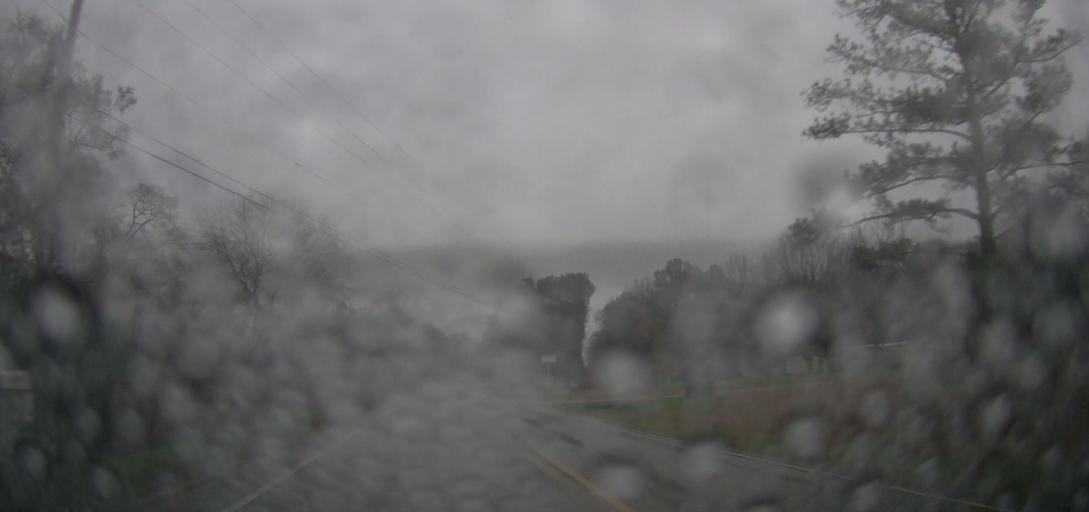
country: US
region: Alabama
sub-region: Autauga County
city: Prattville
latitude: 32.5156
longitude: -86.5939
